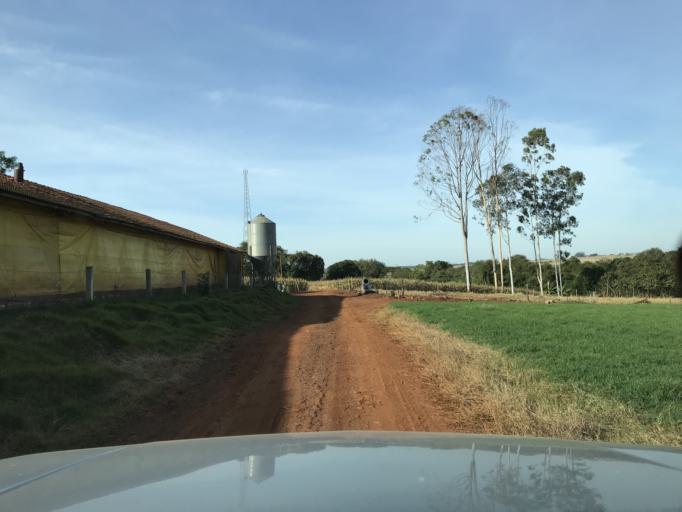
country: BR
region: Parana
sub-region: Palotina
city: Palotina
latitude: -24.2479
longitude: -53.7461
